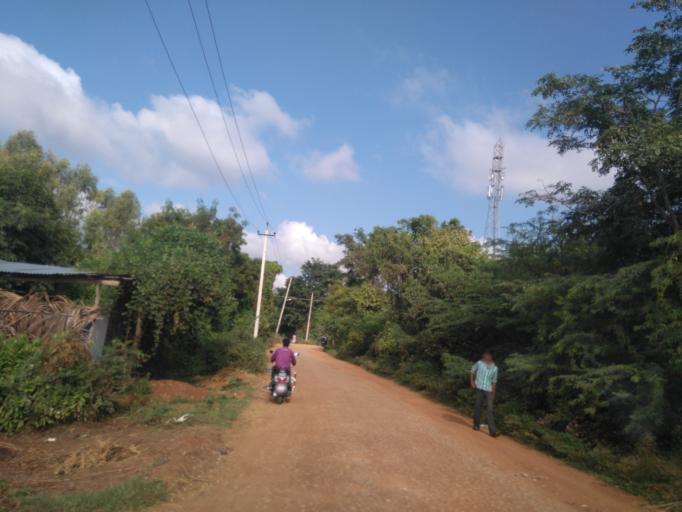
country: IN
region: Karnataka
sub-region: Mysore
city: Tirumakudal Narsipur
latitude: 12.2593
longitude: 76.9730
